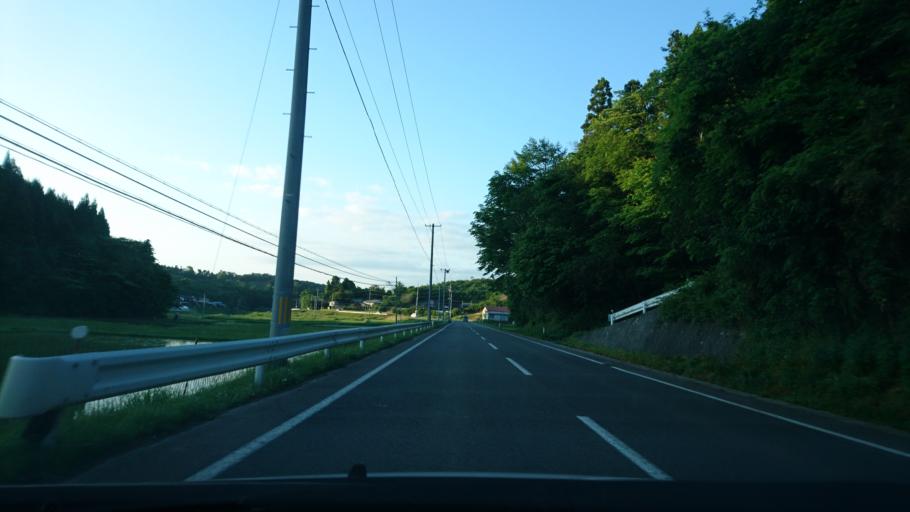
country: JP
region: Iwate
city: Ichinoseki
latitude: 38.8863
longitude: 141.1569
